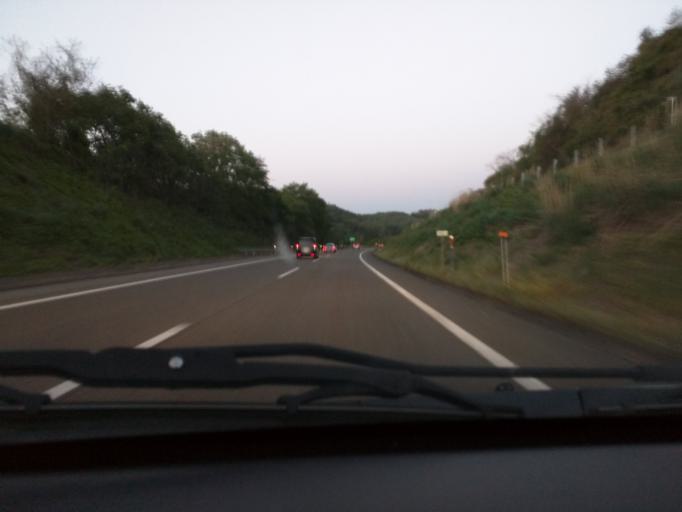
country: JP
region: Niigata
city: Kashiwazaki
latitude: 37.3398
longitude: 138.5251
